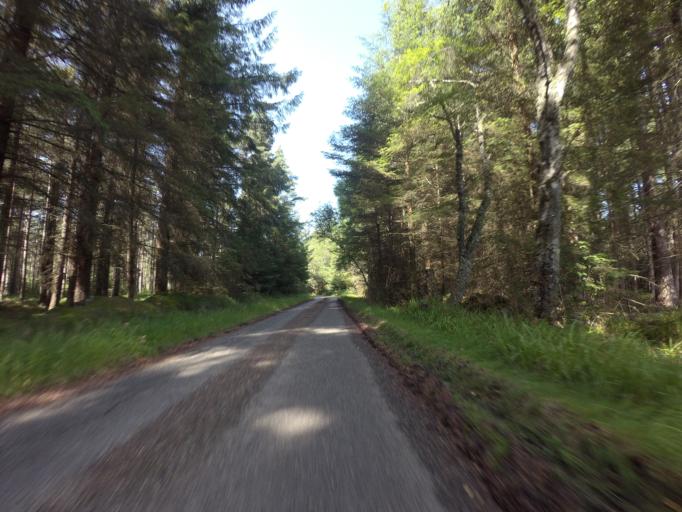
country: GB
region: Scotland
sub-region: Highland
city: Nairn
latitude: 57.5019
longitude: -3.9281
